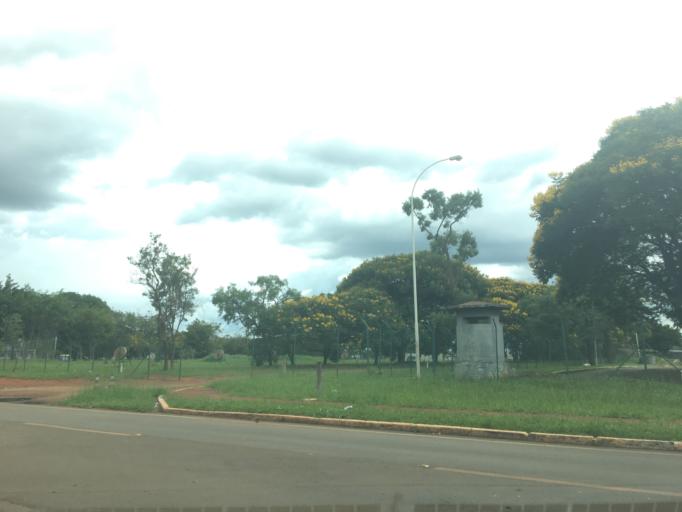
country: BR
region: Federal District
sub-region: Brasilia
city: Brasilia
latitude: -15.8255
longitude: -47.9406
